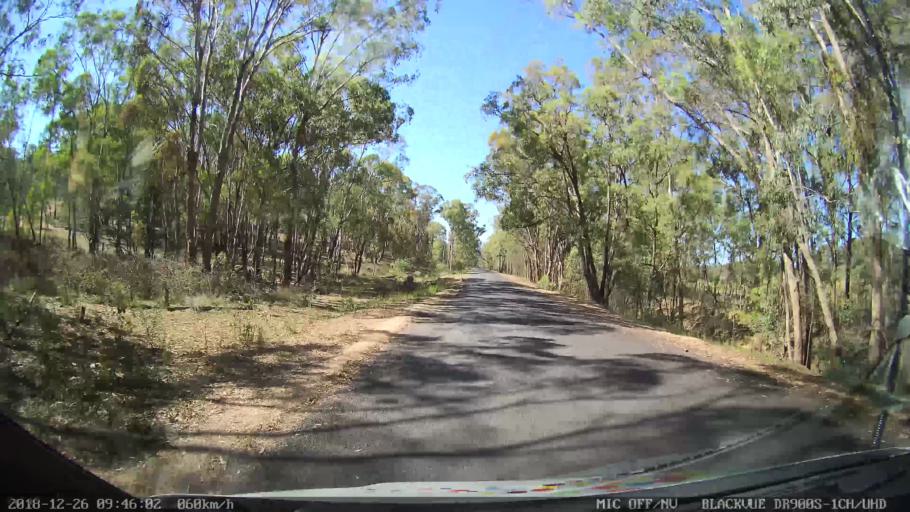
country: AU
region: New South Wales
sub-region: Mid-Western Regional
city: Kandos
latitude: -32.9660
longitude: 150.1059
